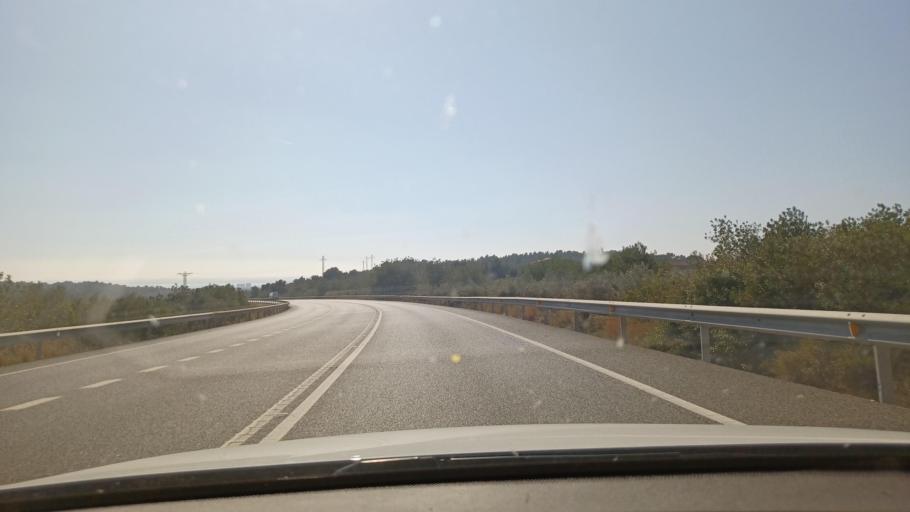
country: ES
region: Catalonia
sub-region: Provincia de Tarragona
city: El Perello
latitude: 40.8537
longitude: 0.7130
